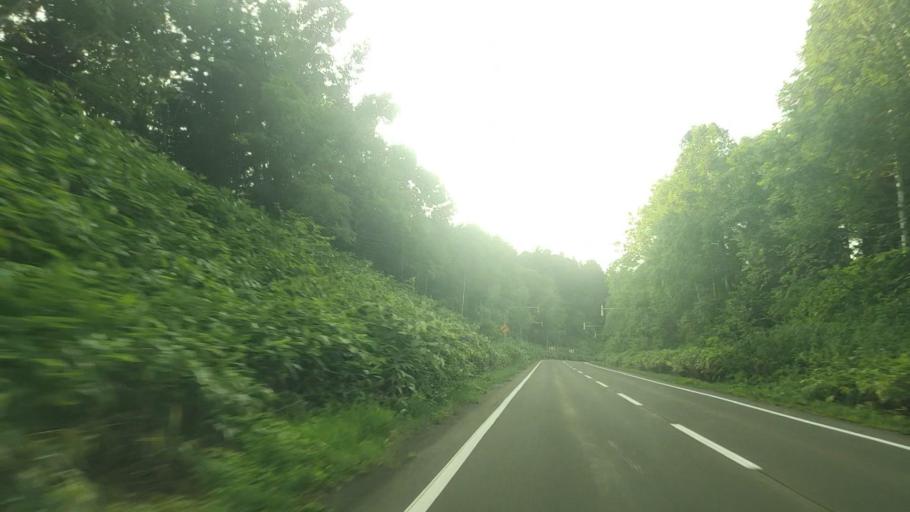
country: JP
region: Hokkaido
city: Bibai
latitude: 43.1411
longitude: 142.0933
